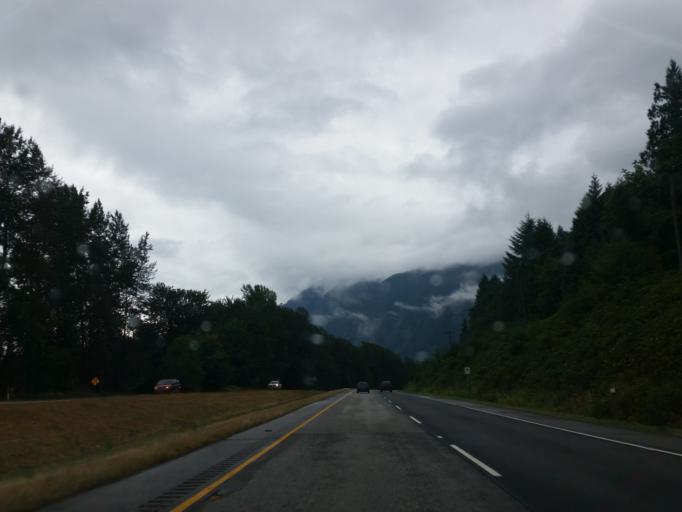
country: CA
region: British Columbia
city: Agassiz
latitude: 49.2097
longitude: -121.7075
